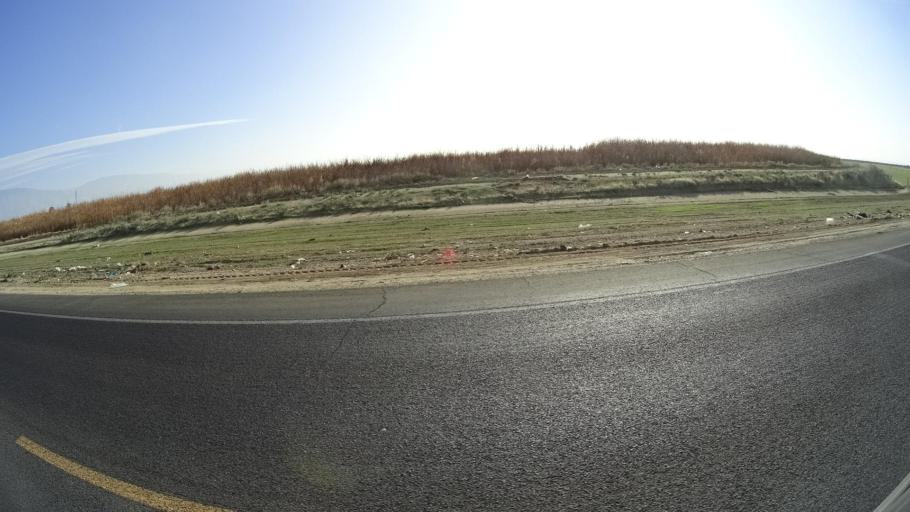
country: US
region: California
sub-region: Kern County
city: Arvin
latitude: 35.3336
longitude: -118.8119
